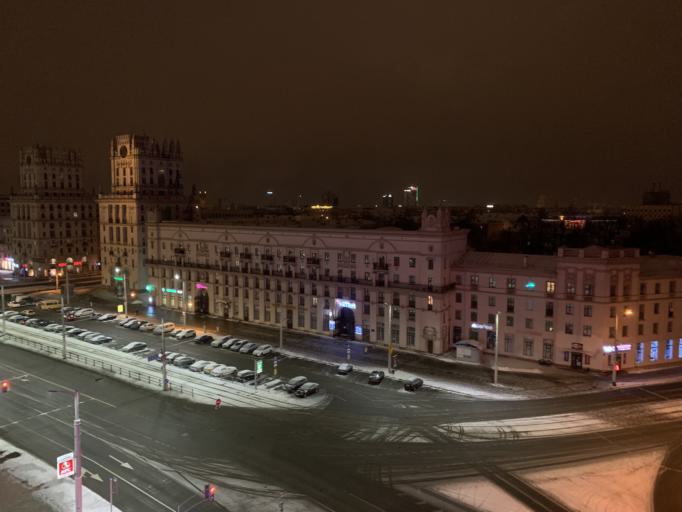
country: BY
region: Minsk
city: Minsk
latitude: 53.8905
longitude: 27.5537
